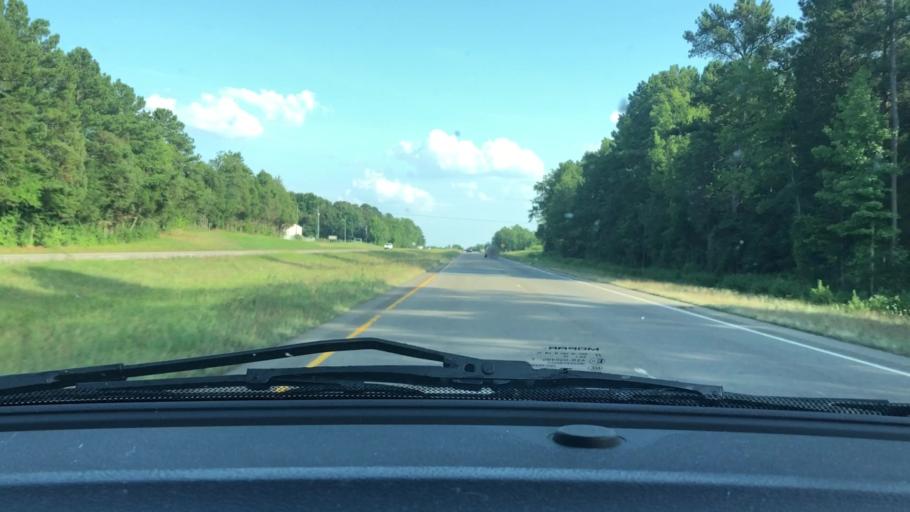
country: US
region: North Carolina
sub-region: Chatham County
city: Farmville
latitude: 35.5823
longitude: -79.3122
